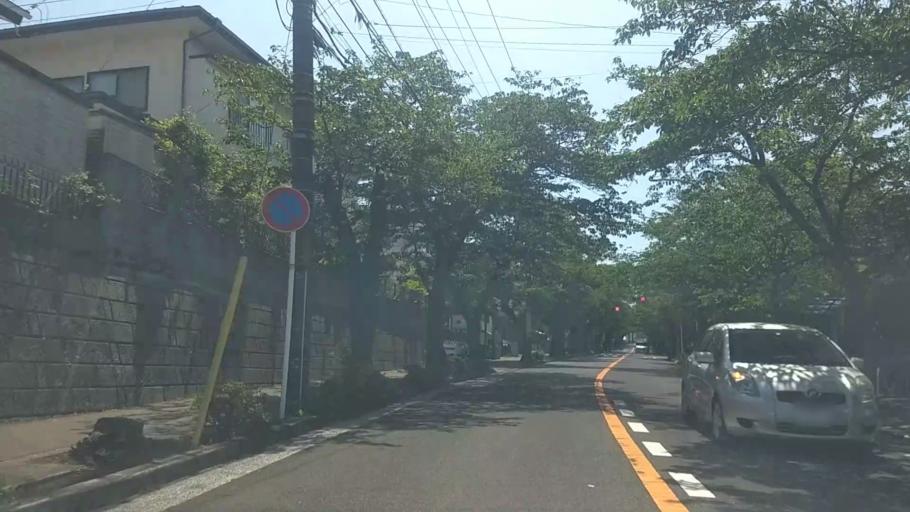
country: JP
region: Kanagawa
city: Zushi
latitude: 35.3089
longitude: 139.5757
